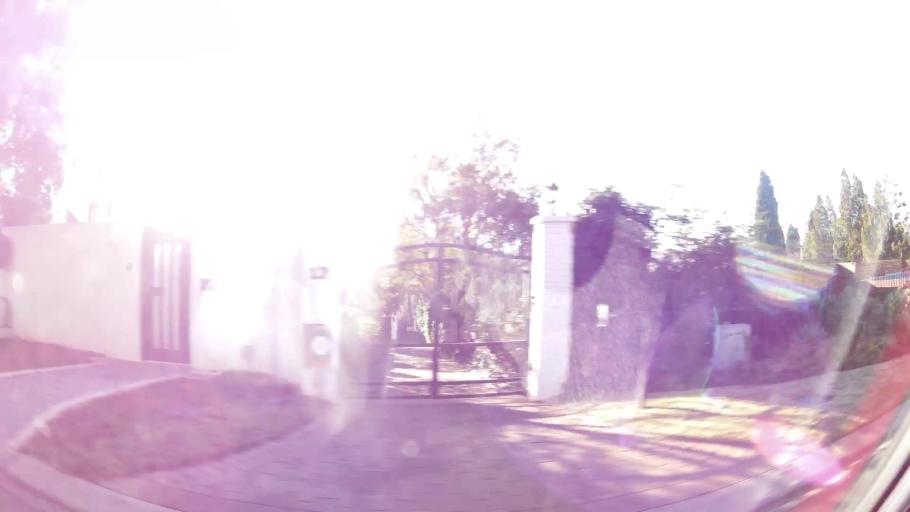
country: ZA
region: Gauteng
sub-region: City of Johannesburg Metropolitan Municipality
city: Midrand
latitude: -26.0285
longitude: 28.0546
